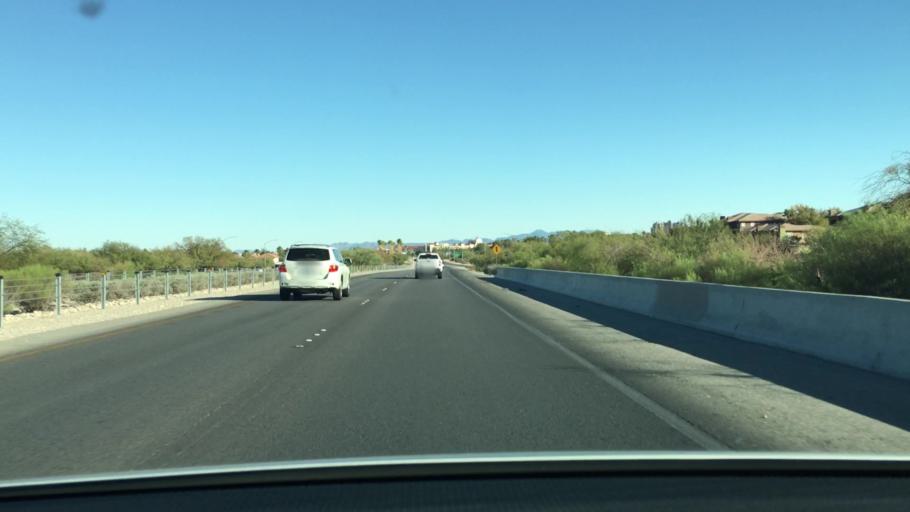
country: US
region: Nevada
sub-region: Clark County
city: Summerlin South
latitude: 36.1861
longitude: -115.3058
